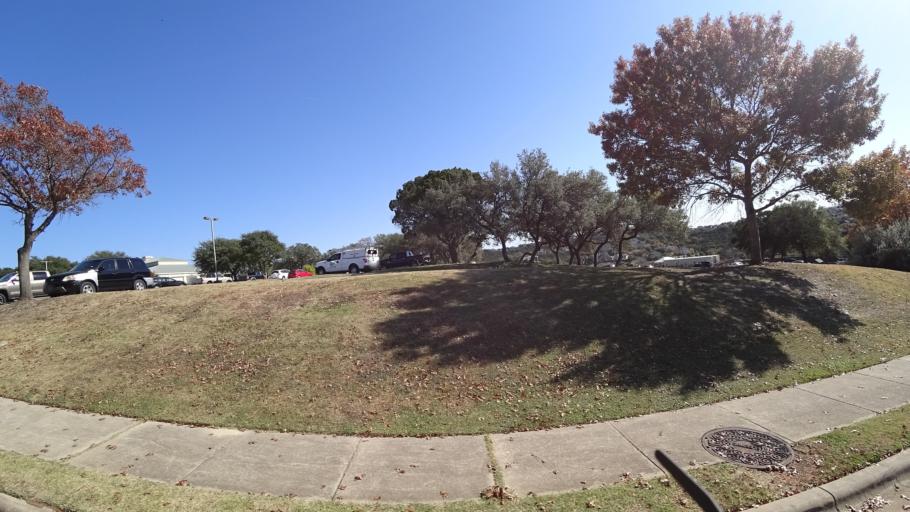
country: US
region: Texas
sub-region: Travis County
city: Lost Creek
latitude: 30.3684
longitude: -97.8618
